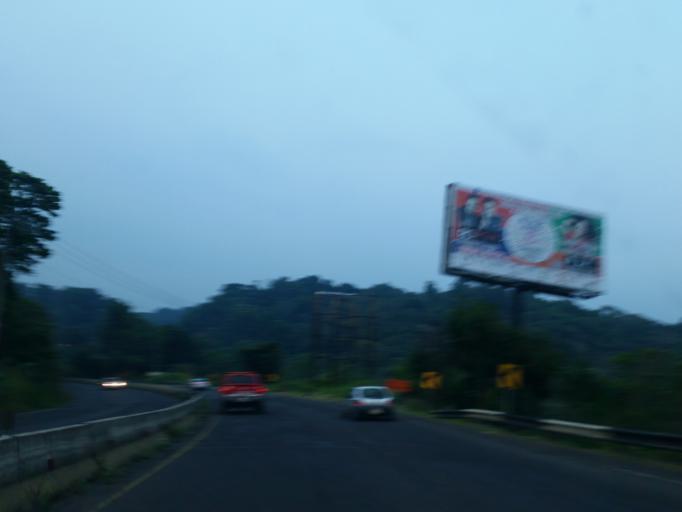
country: MX
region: Veracruz
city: Coatepec
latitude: 19.4901
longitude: -96.9370
